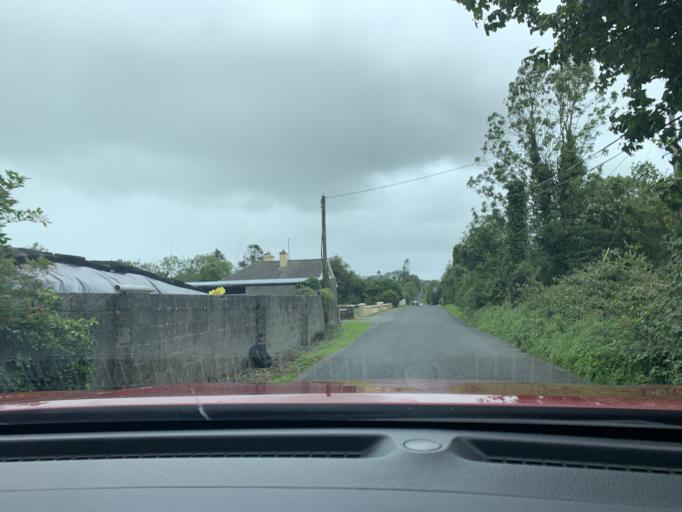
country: IE
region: Connaught
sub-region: County Leitrim
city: Carrick-on-Shannon
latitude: 53.8602
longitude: -8.1438
